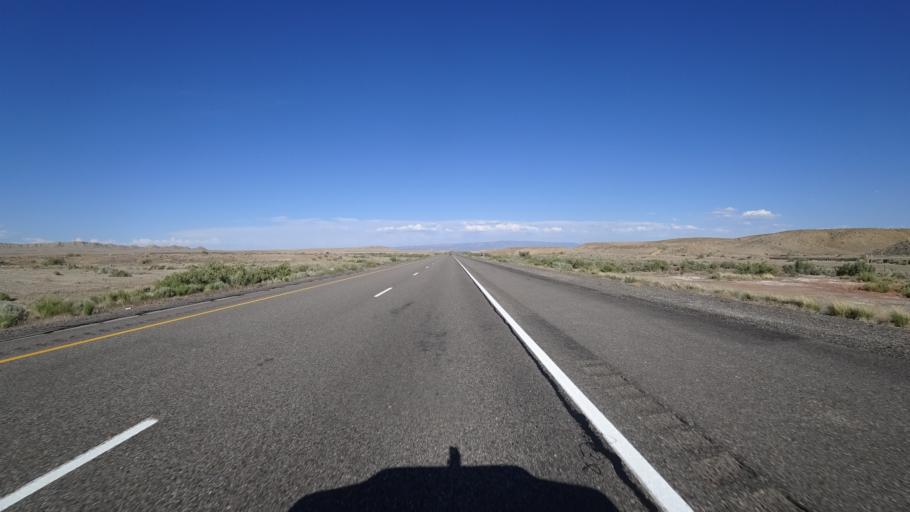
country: US
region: Utah
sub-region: Grand County
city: Moab
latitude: 38.9403
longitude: -109.5221
